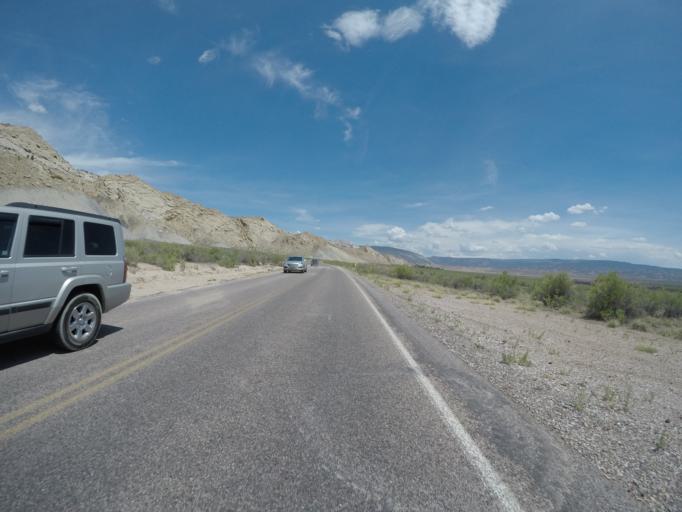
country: US
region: Utah
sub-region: Uintah County
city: Naples
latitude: 40.4379
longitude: -109.3201
